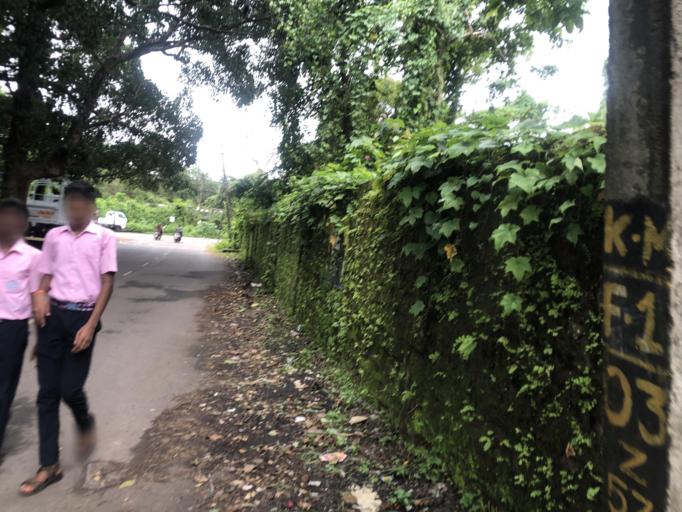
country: IN
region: Goa
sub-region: North Goa
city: Serula
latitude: 15.5394
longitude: 73.8316
